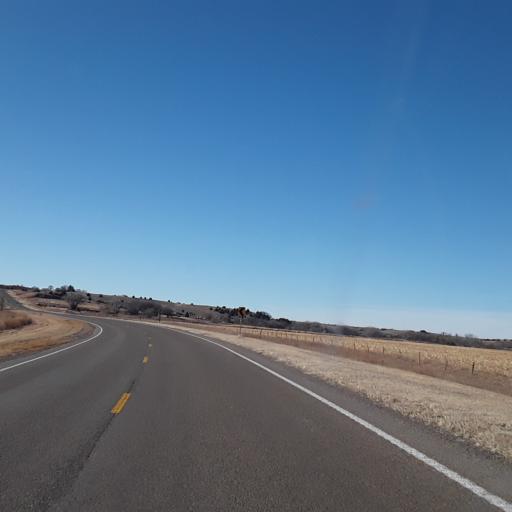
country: US
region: Nebraska
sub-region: Frontier County
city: Stockville
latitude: 40.6326
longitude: -100.5704
